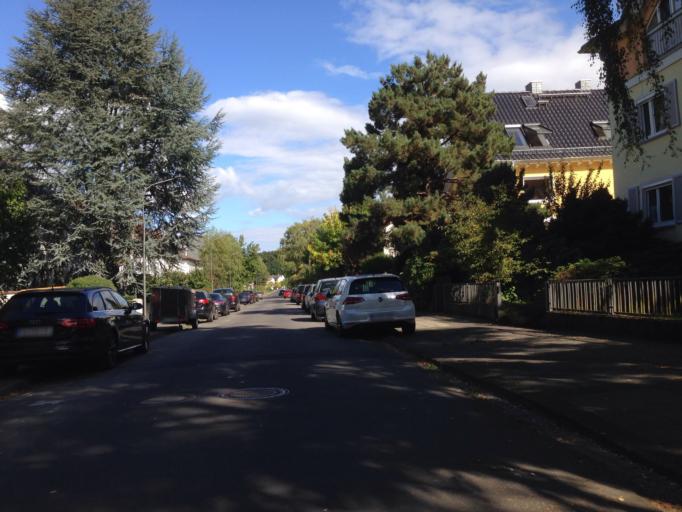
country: DE
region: Hesse
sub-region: Regierungsbezirk Giessen
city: Giessen
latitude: 50.5873
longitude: 8.6908
